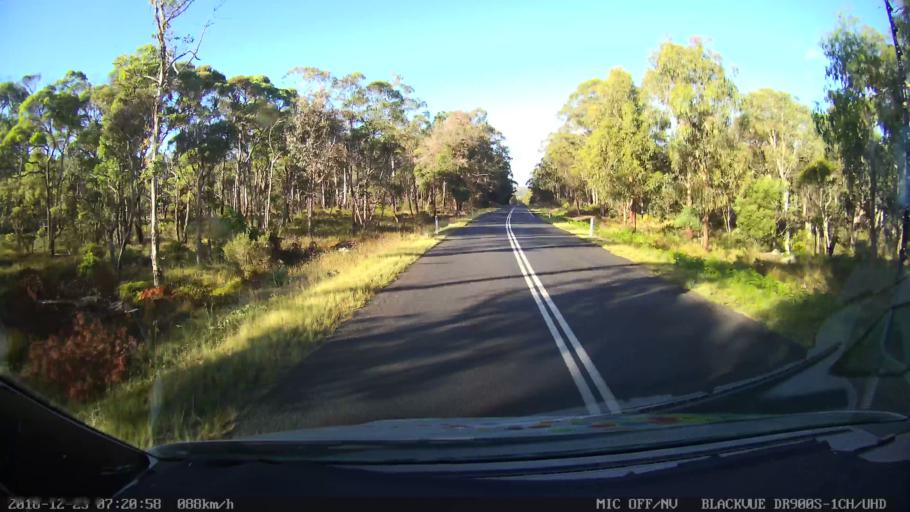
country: AU
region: New South Wales
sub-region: Bellingen
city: Dorrigo
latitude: -30.4947
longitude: 152.2698
